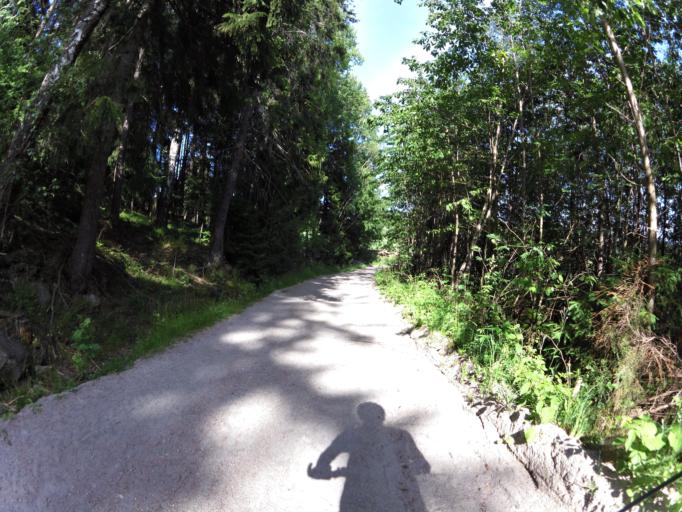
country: NO
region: Ostfold
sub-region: Fredrikstad
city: Fredrikstad
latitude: 59.2478
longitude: 10.9692
